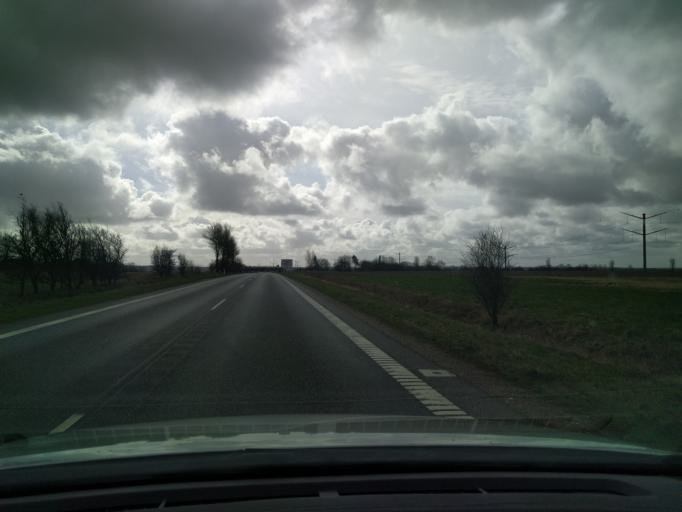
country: DK
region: South Denmark
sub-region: Haderslev Kommune
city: Gram
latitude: 55.2582
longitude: 9.1468
